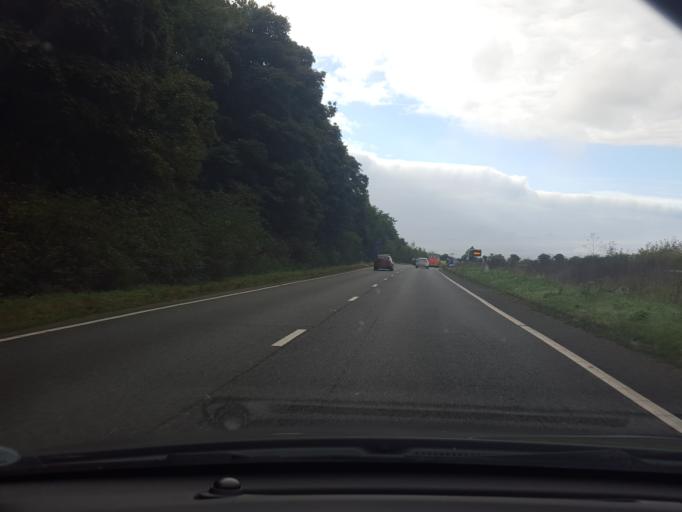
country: GB
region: England
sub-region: Suffolk
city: Great Barton
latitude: 52.2367
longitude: 0.7592
